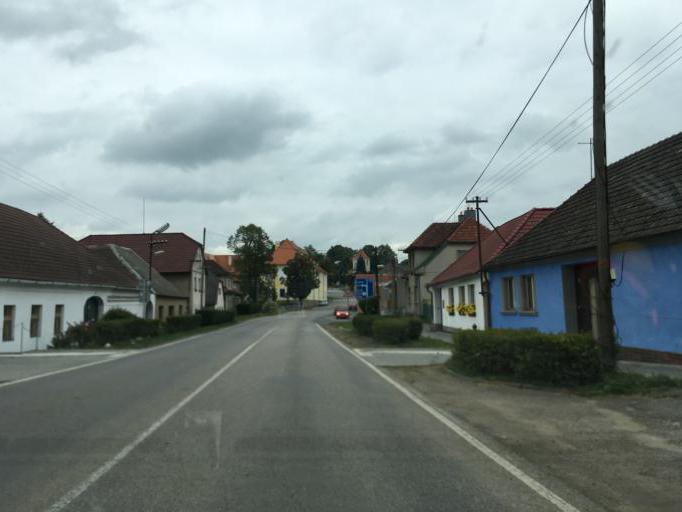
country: CZ
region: Central Bohemia
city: Cechtice
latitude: 49.6258
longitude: 15.0473
